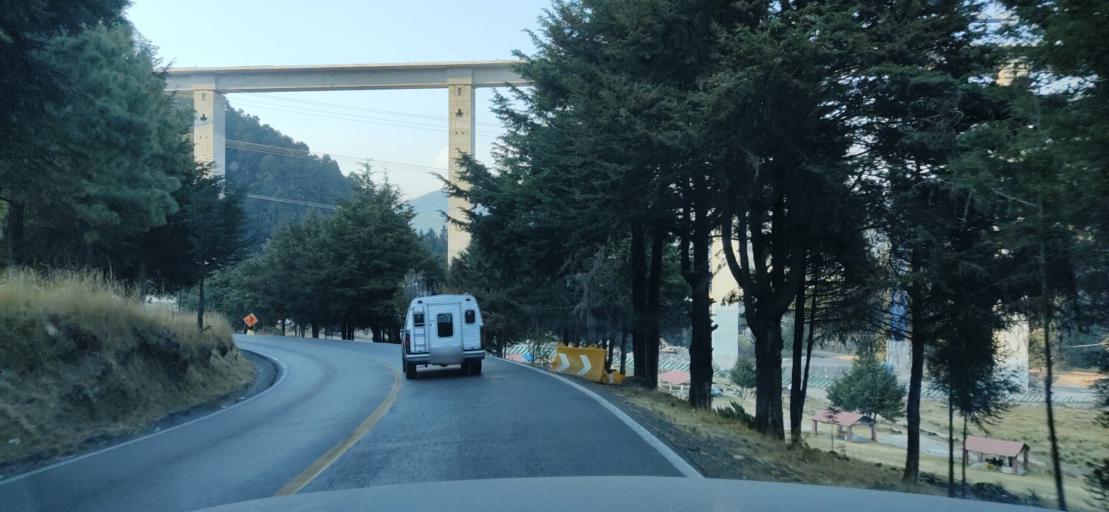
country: MX
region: Mexico
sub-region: Ocoyoacac
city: San Jeronimo Acazulco
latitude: 19.2926
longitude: -99.3748
